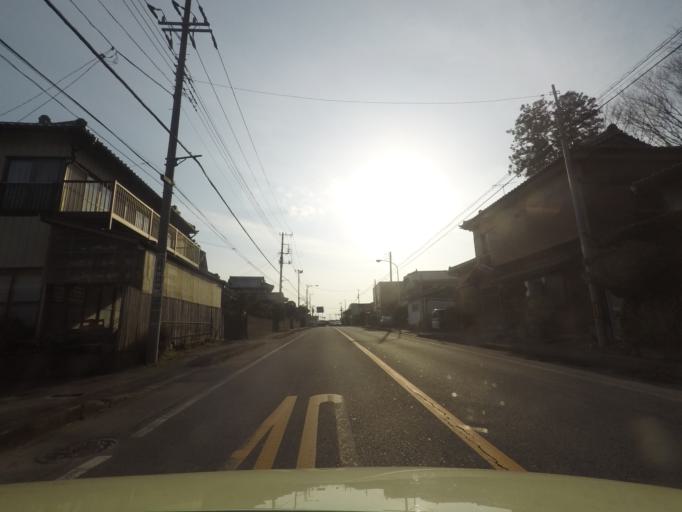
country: JP
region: Ibaraki
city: Okunoya
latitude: 36.2841
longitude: 140.4200
